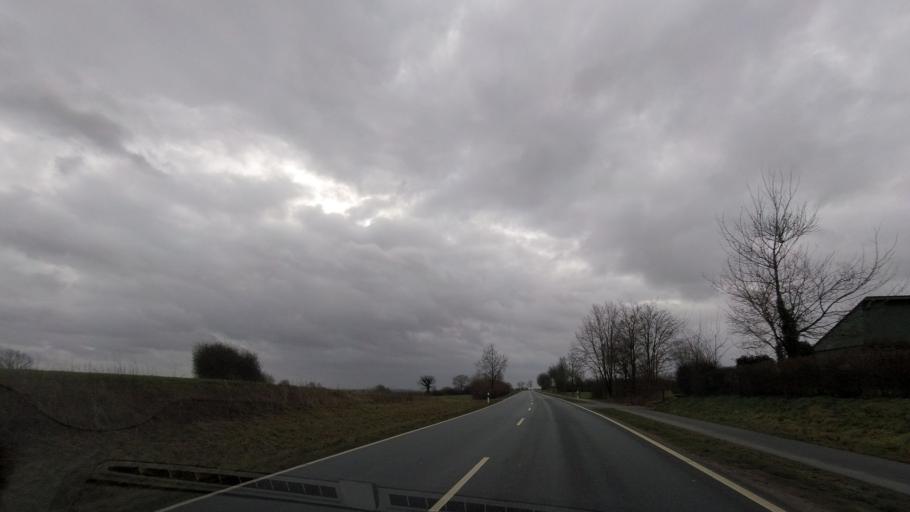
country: DE
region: Schleswig-Holstein
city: Tolk
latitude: 54.5726
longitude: 9.6464
